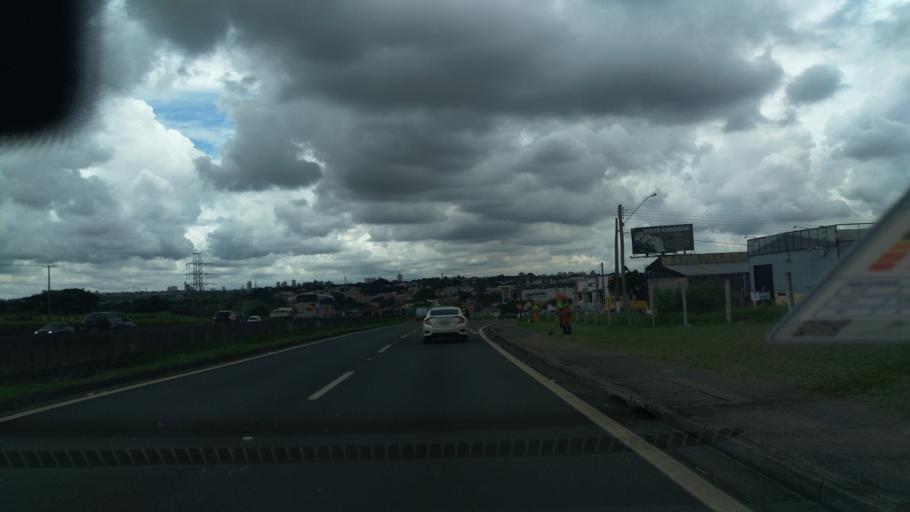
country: BR
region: Sao Paulo
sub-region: Campinas
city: Campinas
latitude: -22.8760
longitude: -47.1227
